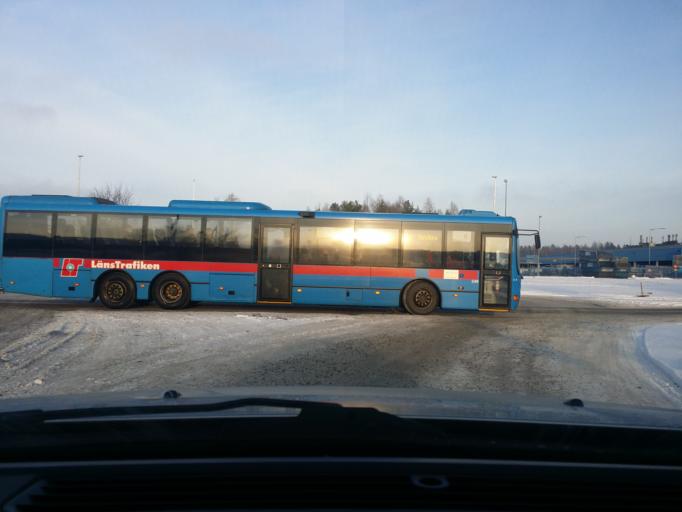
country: SE
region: OErebro
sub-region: Lindesbergs Kommun
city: Lindesberg
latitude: 59.6011
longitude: 15.1944
